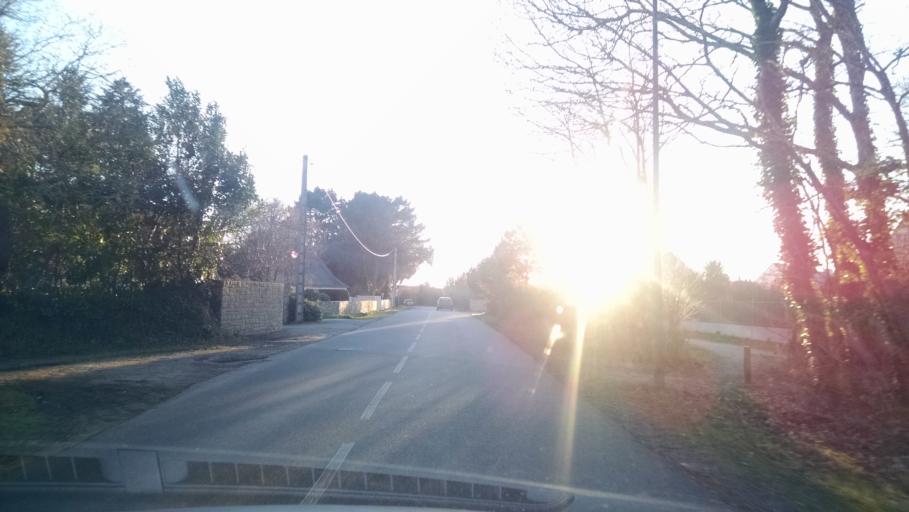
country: FR
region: Brittany
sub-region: Departement du Morbihan
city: Guidel-Plage
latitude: 47.7788
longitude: -3.5138
